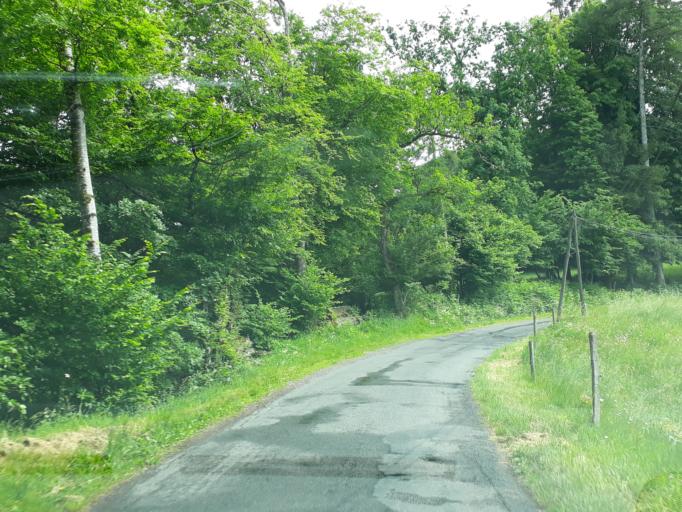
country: FR
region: Limousin
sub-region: Departement de la Correze
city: Beynat
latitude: 45.1193
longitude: 1.7608
